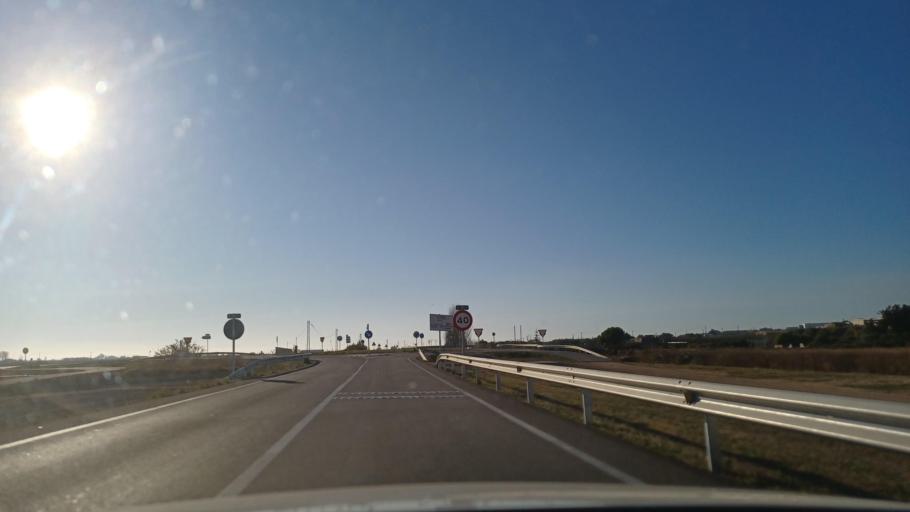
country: ES
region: Catalonia
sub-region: Provincia de Tarragona
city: Sant Carles de la Rapita
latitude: 40.6430
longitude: 0.6002
